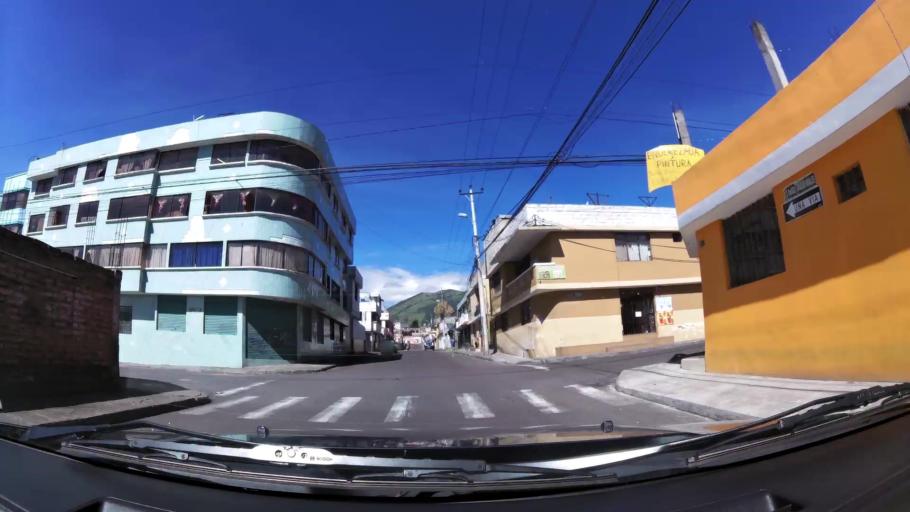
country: EC
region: Pichincha
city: Quito
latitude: -0.2838
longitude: -78.5600
